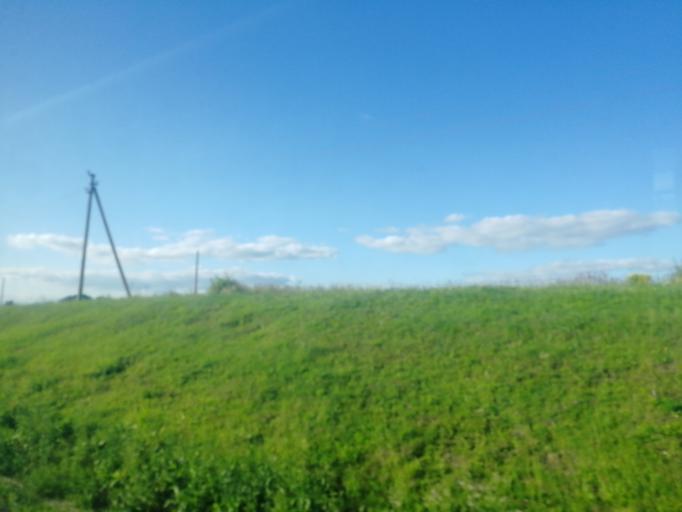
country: RU
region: Tula
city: Leninskiy
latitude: 54.2442
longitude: 37.3298
